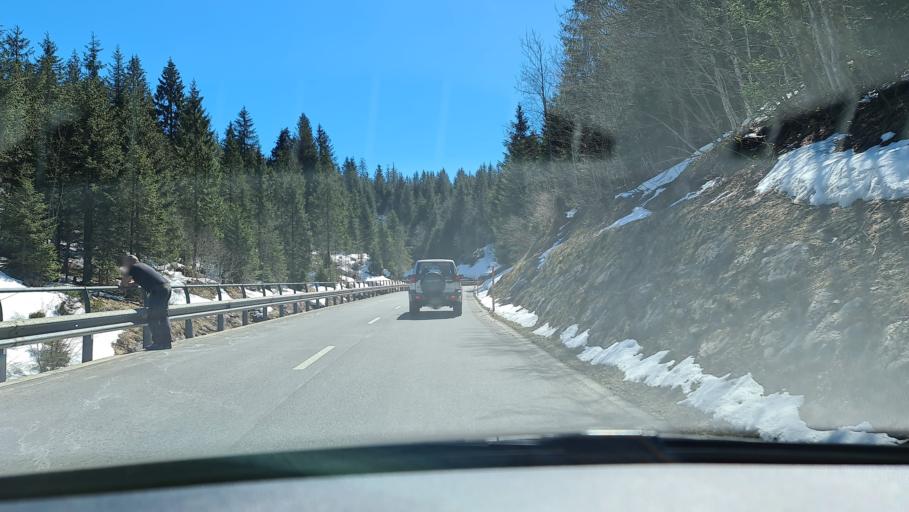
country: CH
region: Schwyz
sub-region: Bezirk Schwyz
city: Schwyz
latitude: 47.0504
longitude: 8.7075
